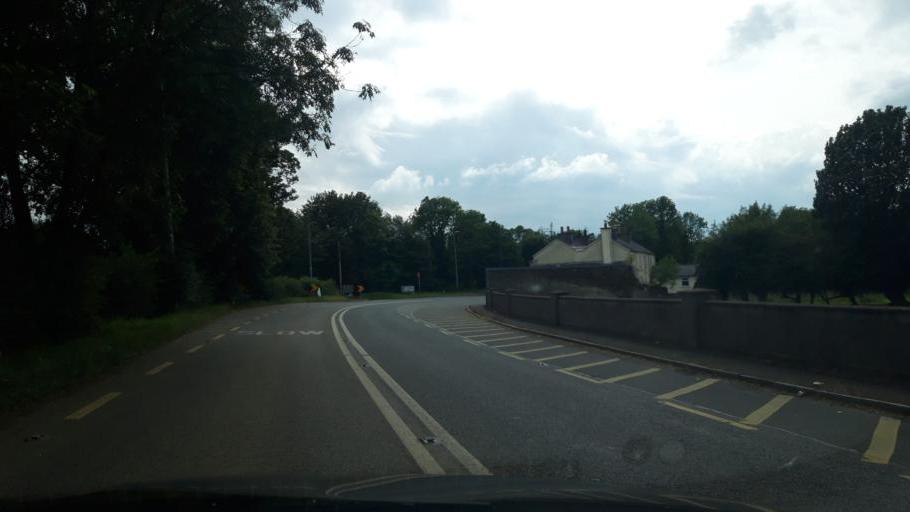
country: IE
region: Leinster
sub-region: Kilkenny
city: Castlecomer
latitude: 52.8429
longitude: -7.1296
